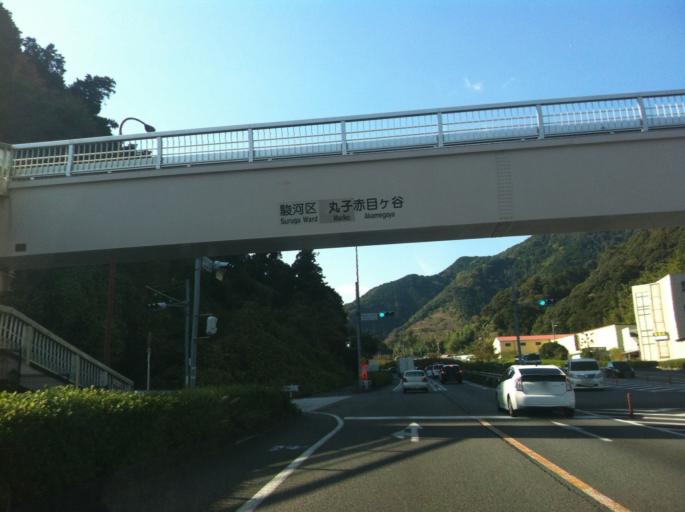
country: JP
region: Shizuoka
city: Shizuoka-shi
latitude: 34.9414
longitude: 138.3234
